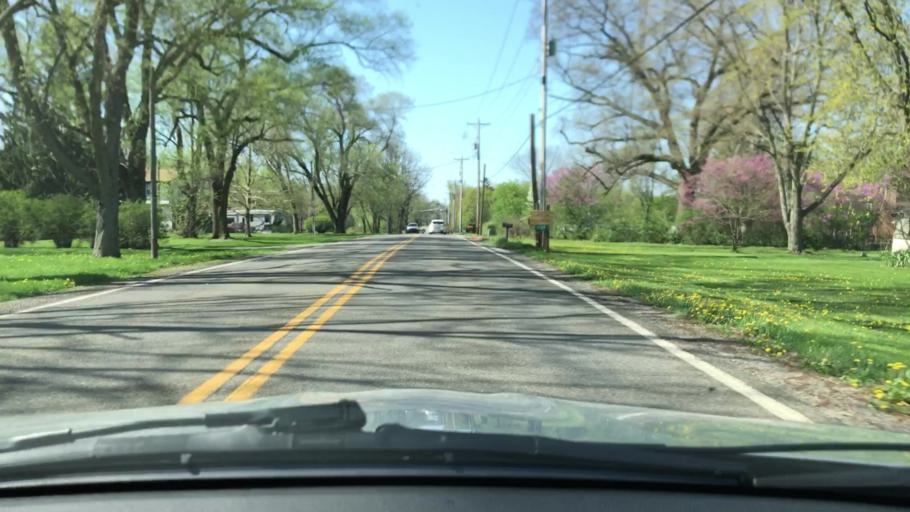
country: US
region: Indiana
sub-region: Saint Joseph County
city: Georgetown
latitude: 41.7485
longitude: -86.2995
